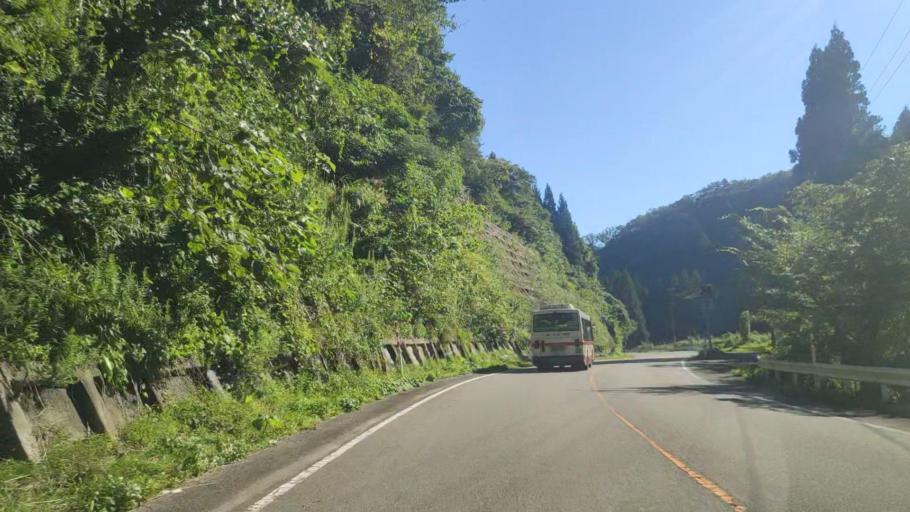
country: JP
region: Ishikawa
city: Nanao
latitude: 37.2405
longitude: 136.9796
